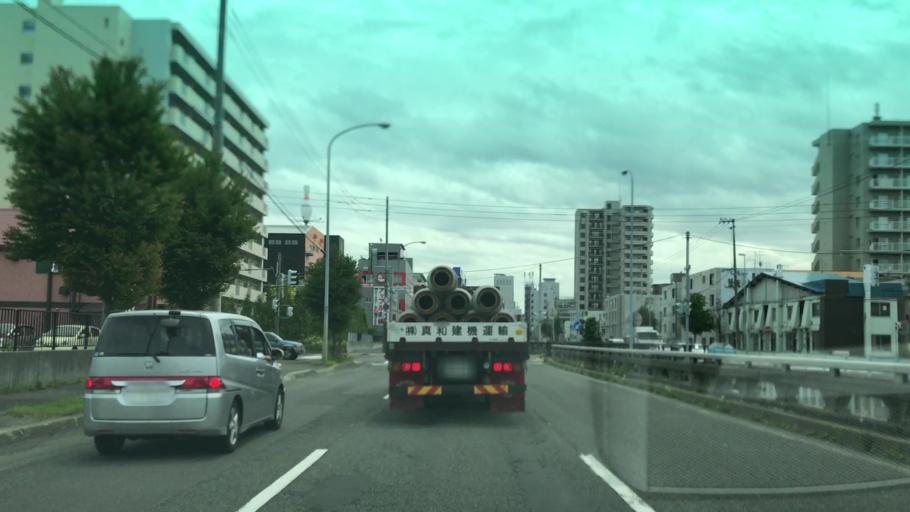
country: JP
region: Hokkaido
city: Sapporo
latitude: 43.0884
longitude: 141.3485
